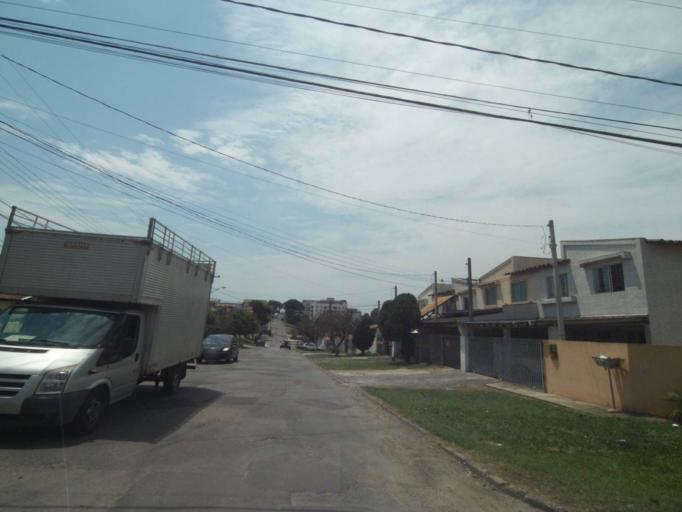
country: BR
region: Parana
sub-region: Pinhais
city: Pinhais
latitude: -25.3989
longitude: -49.2114
